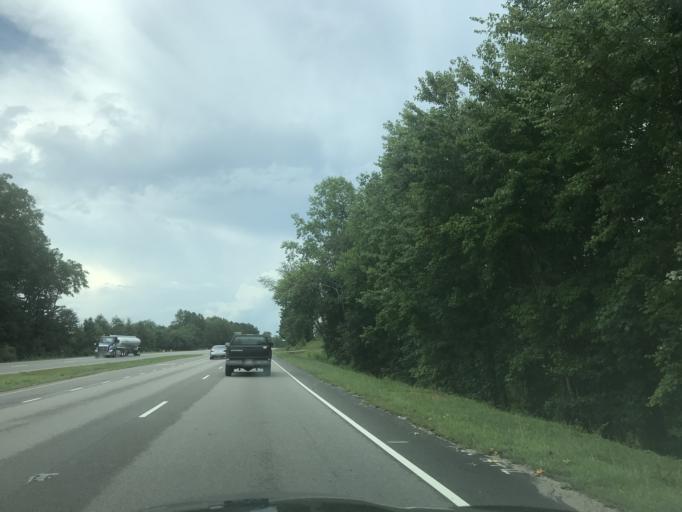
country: US
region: North Carolina
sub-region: Wake County
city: Garner
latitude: 35.6834
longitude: -78.5375
